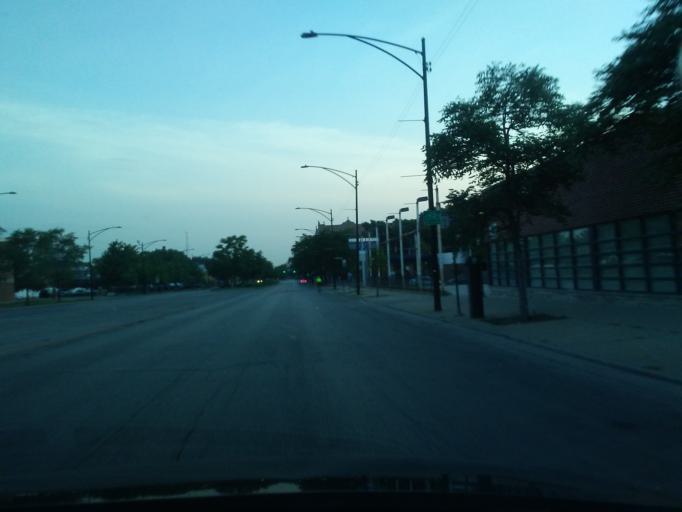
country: US
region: Illinois
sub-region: Cook County
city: Evanston
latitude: 41.9910
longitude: -87.6699
